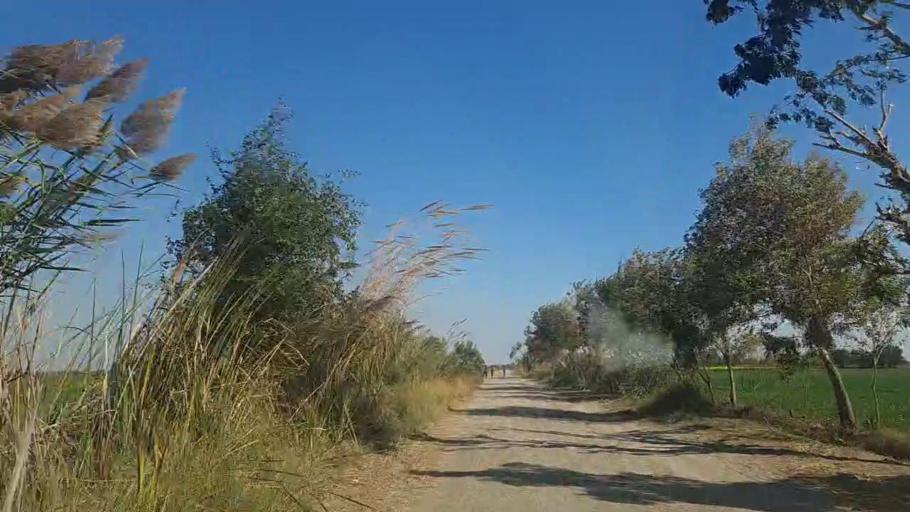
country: PK
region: Sindh
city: Sanghar
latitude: 26.2093
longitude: 68.8956
